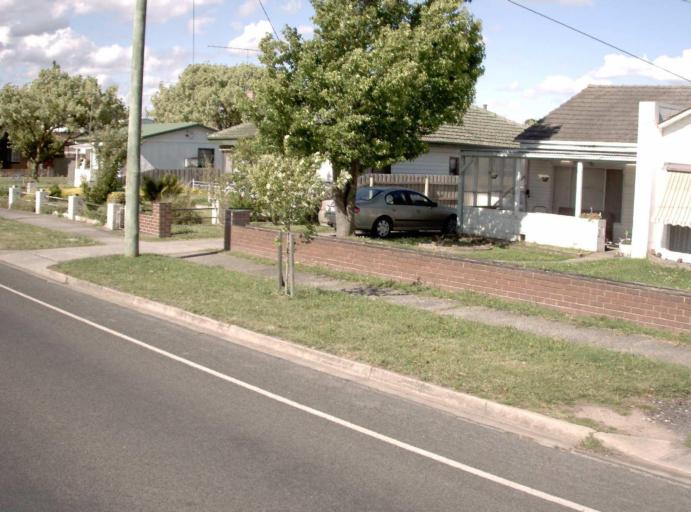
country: AU
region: Victoria
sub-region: Latrobe
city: Morwell
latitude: -38.2308
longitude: 146.3955
